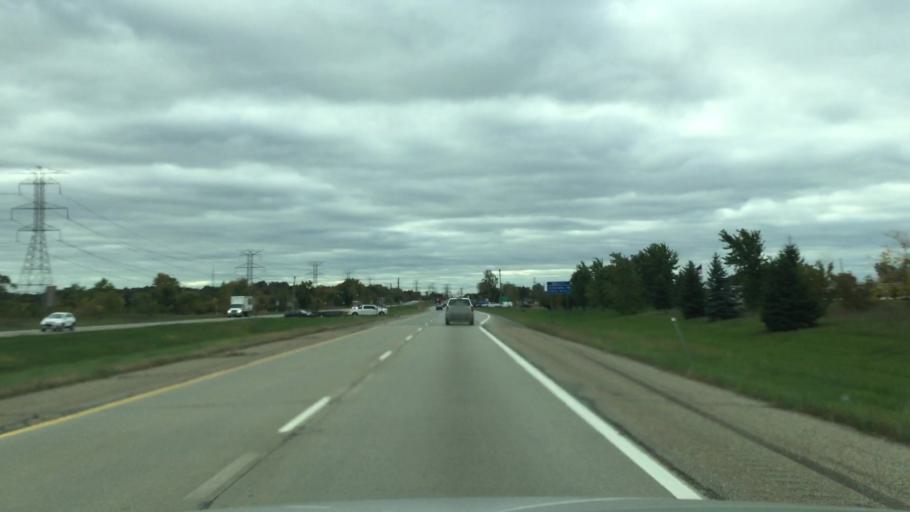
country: US
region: Michigan
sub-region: Macomb County
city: Romeo
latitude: 42.7757
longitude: -83.0096
